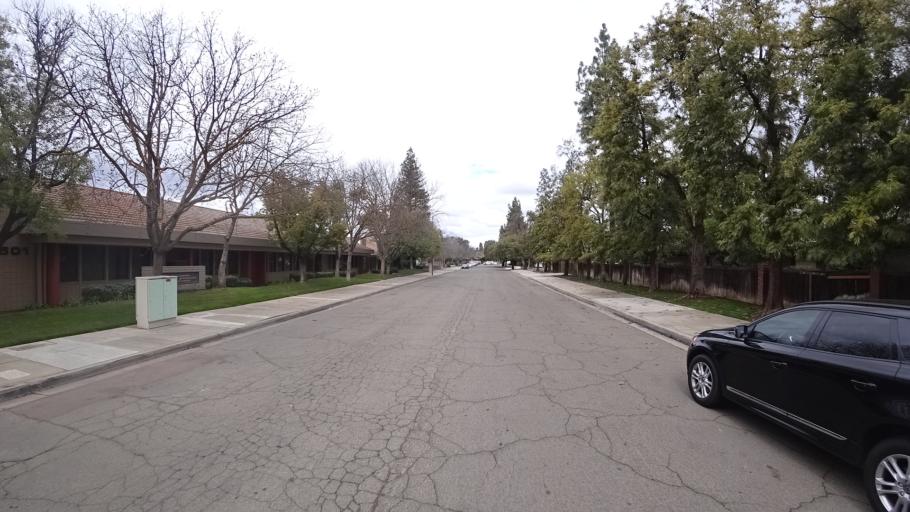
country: US
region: California
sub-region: Fresno County
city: Fresno
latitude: 36.8068
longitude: -119.8355
